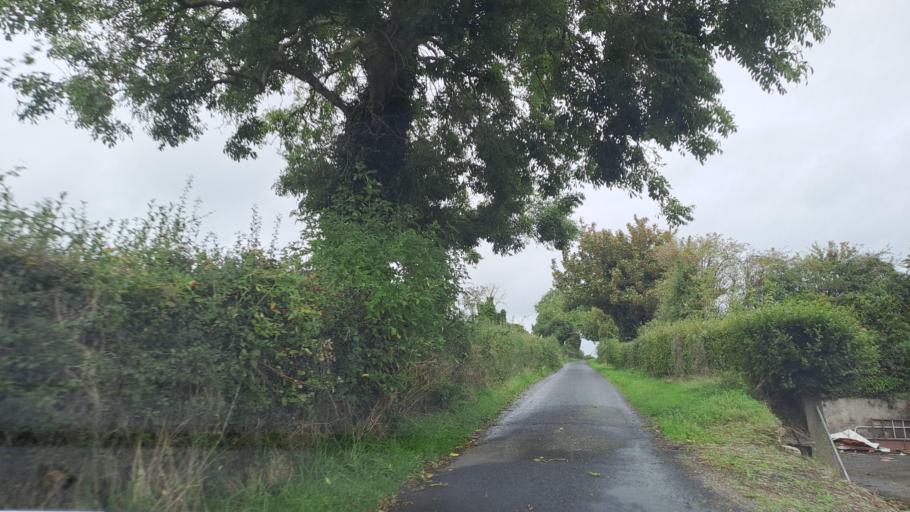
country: IE
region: Ulster
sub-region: County Monaghan
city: Carrickmacross
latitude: 53.9636
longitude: -6.7573
